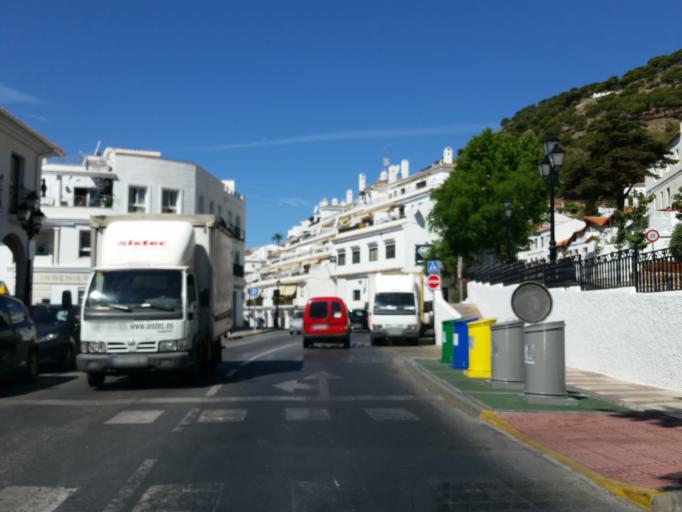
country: ES
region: Andalusia
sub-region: Provincia de Malaga
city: Mijas
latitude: 36.5979
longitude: -4.6357
